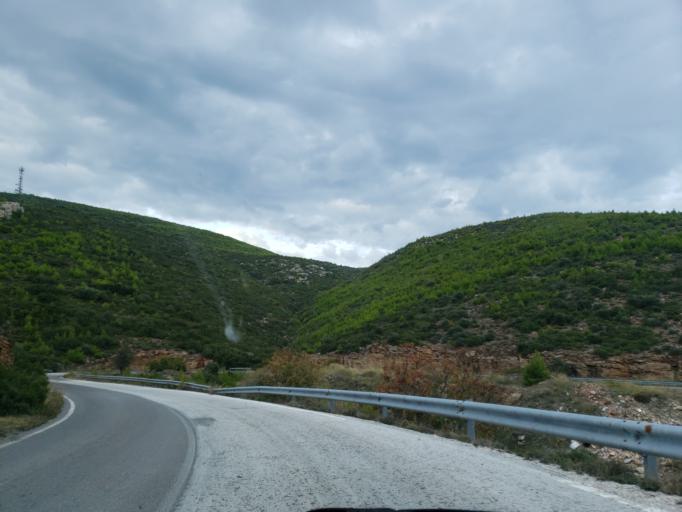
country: GR
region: Attica
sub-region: Nomarchia Anatolikis Attikis
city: Grammatiko
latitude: 38.2104
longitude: 23.9462
